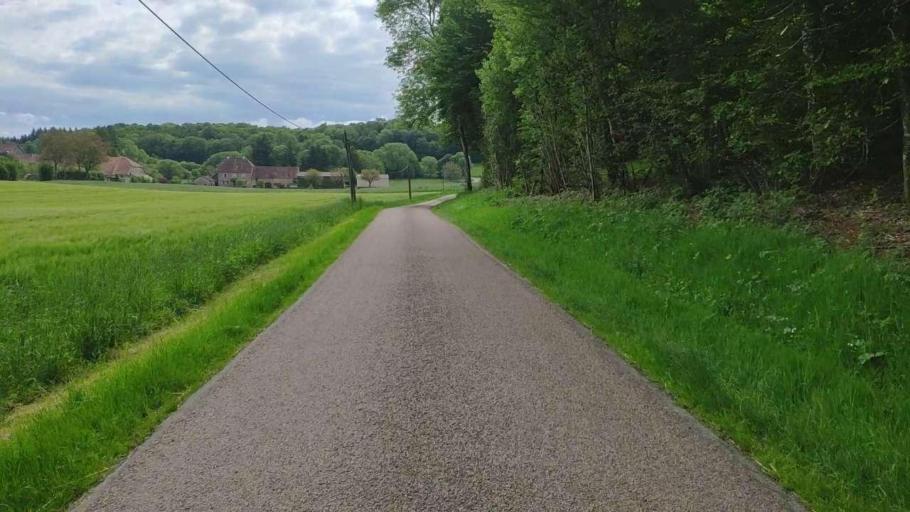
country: FR
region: Franche-Comte
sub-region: Departement du Jura
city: Poligny
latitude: 46.7750
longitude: 5.6492
